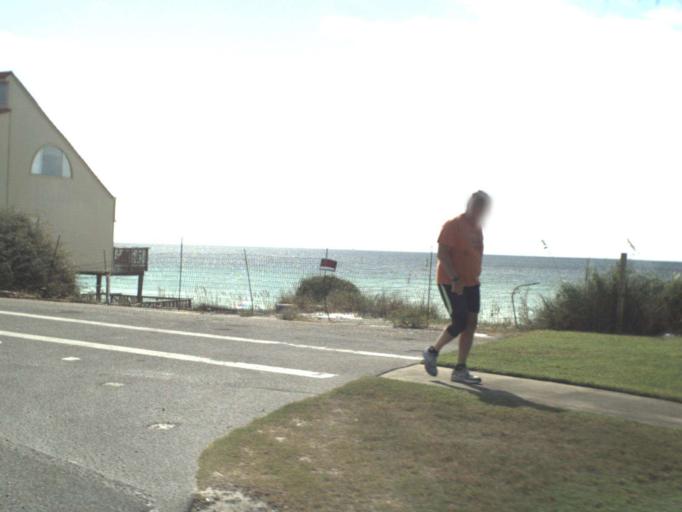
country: US
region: Florida
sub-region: Walton County
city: Miramar Beach
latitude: 30.3800
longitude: -86.4008
